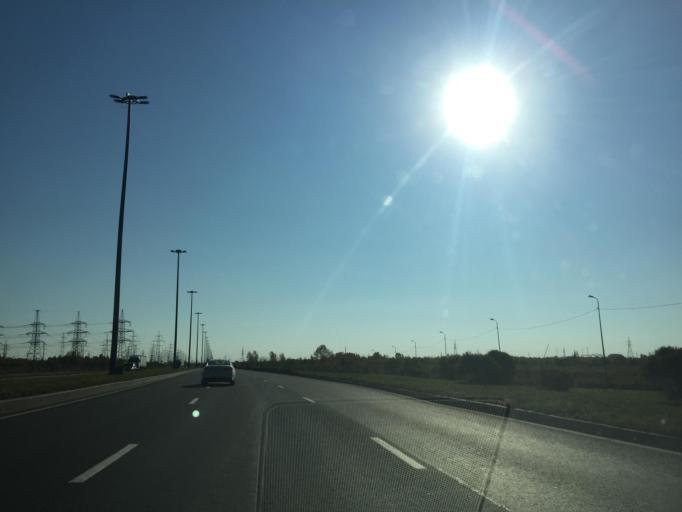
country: RU
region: St.-Petersburg
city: Petro-Slavyanka
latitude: 59.7655
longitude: 30.5033
